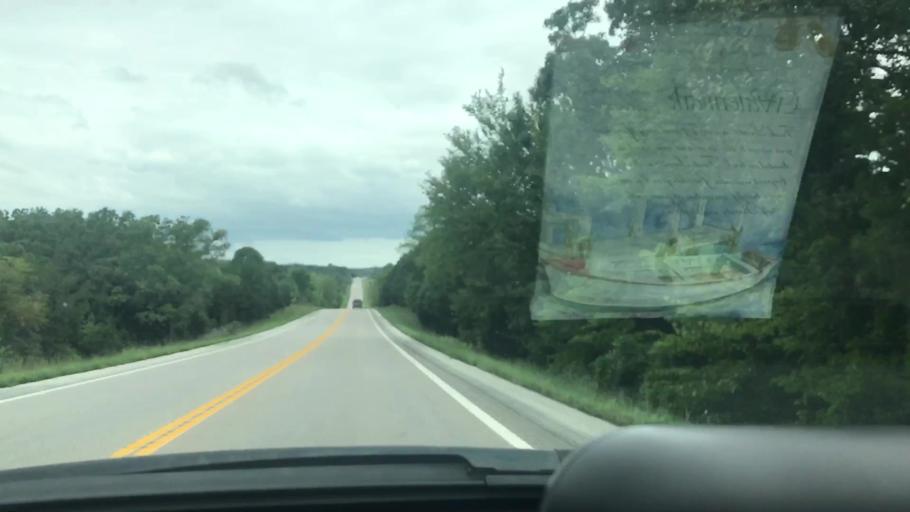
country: US
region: Missouri
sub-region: Dallas County
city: Buffalo
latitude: 37.7140
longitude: -93.1173
